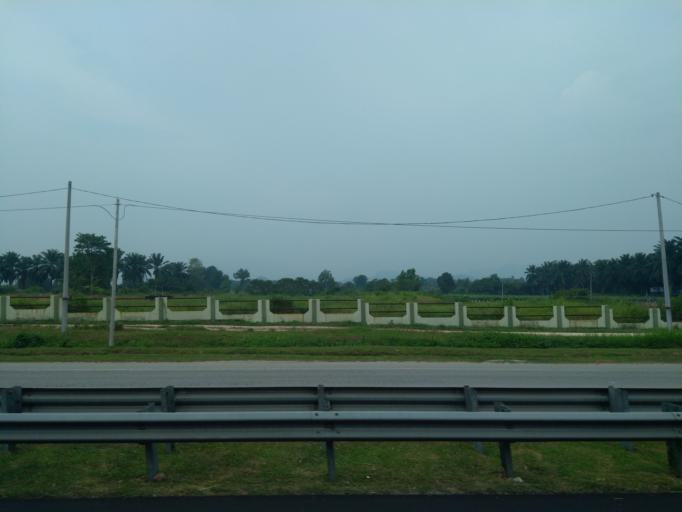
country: MY
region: Perak
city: Ipoh
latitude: 4.6613
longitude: 101.0896
